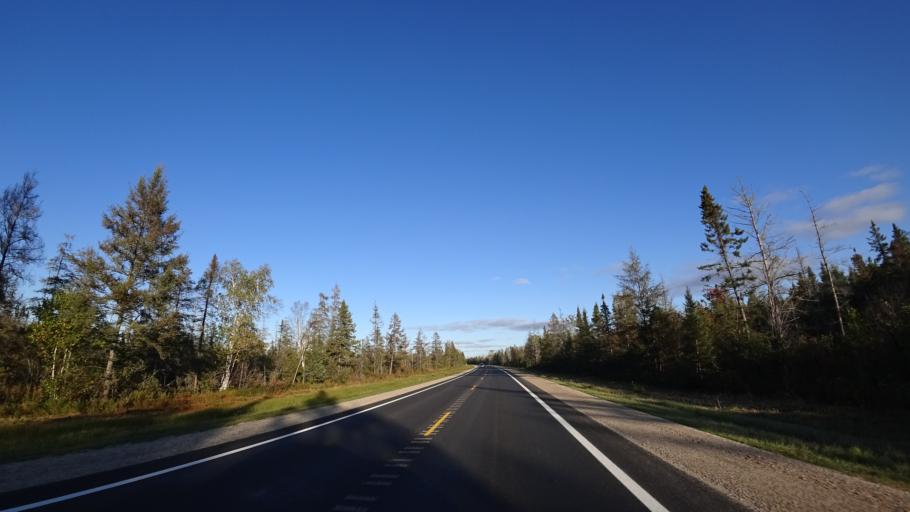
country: US
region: Michigan
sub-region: Luce County
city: Newberry
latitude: 46.3356
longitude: -85.8542
